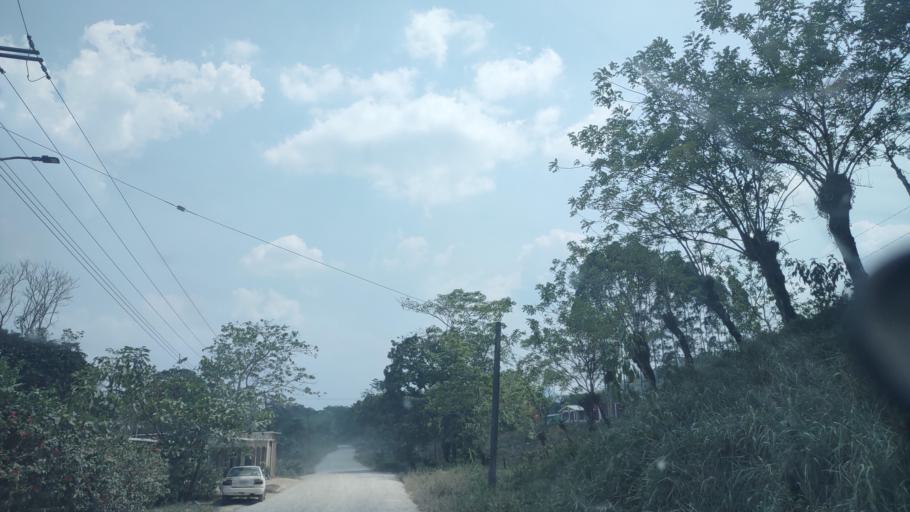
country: MX
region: Tabasco
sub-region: Huimanguillo
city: Francisco Rueda
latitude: 17.5998
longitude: -93.8998
